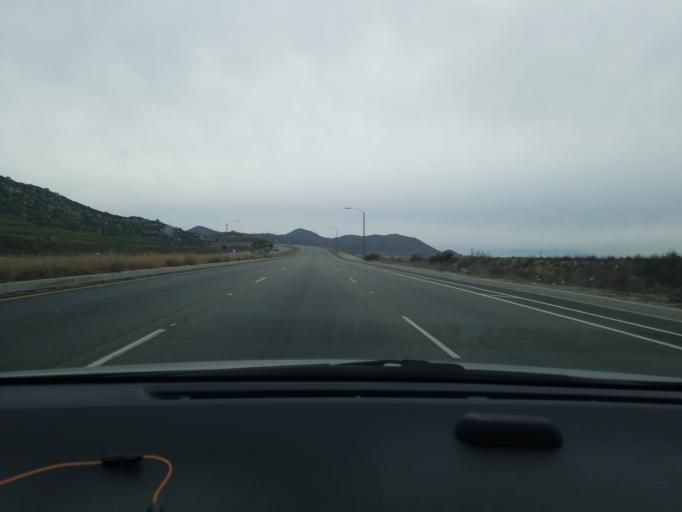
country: US
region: California
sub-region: Riverside County
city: Menifee
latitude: 33.6932
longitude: -117.1295
